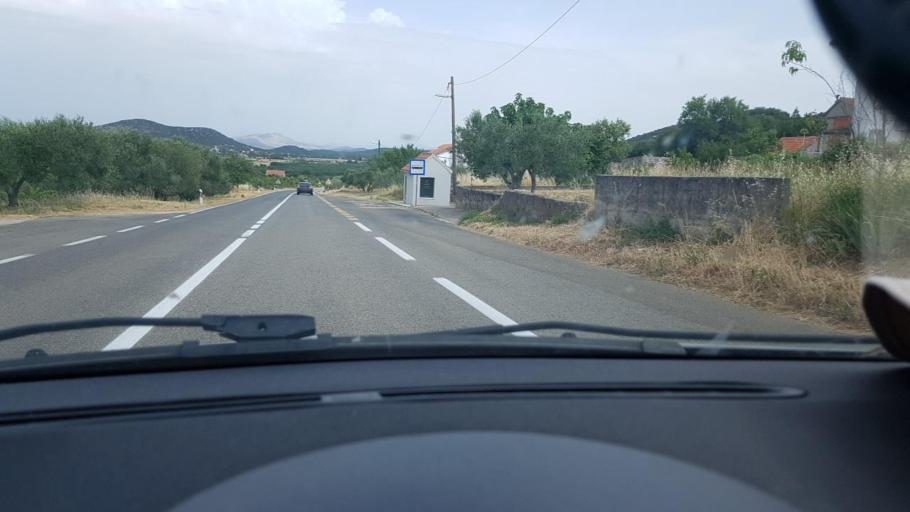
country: HR
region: Sibensko-Kniniska
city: Zaton
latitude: 43.8540
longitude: 15.7613
